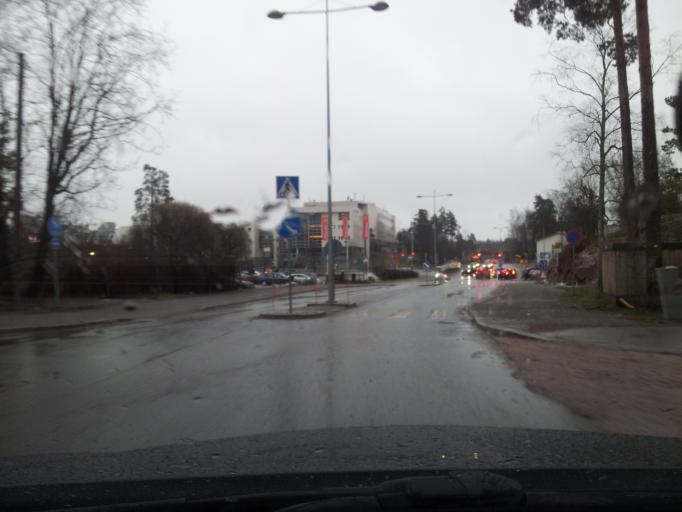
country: FI
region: Uusimaa
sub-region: Helsinki
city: Koukkuniemi
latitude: 60.1638
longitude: 24.7206
